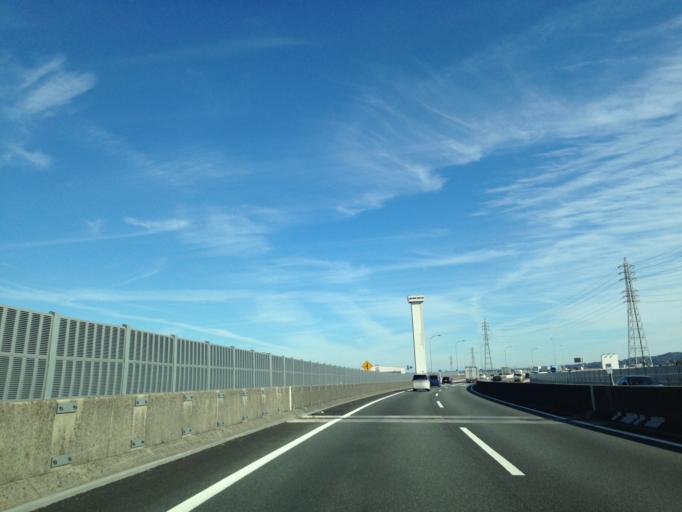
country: JP
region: Shizuoka
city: Fukuroi
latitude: 34.7578
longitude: 137.9241
